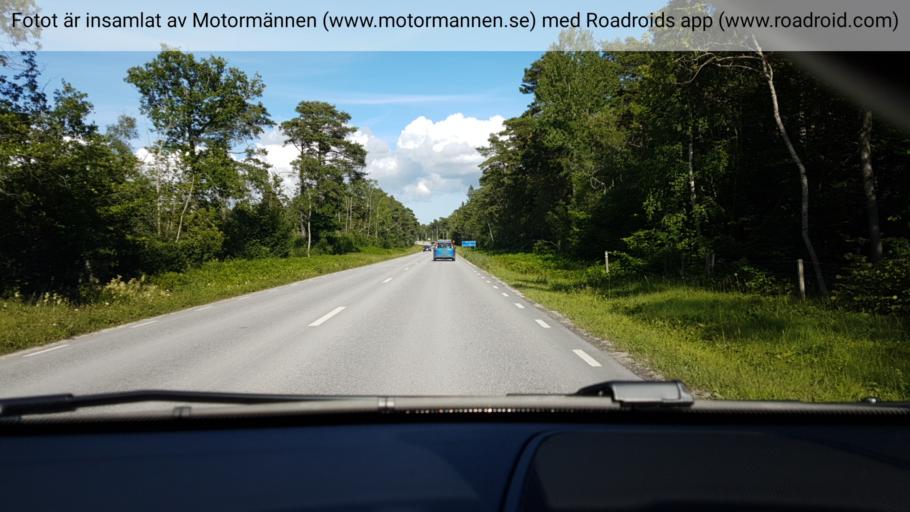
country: SE
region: Gotland
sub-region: Gotland
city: Slite
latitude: 57.7500
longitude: 18.7215
